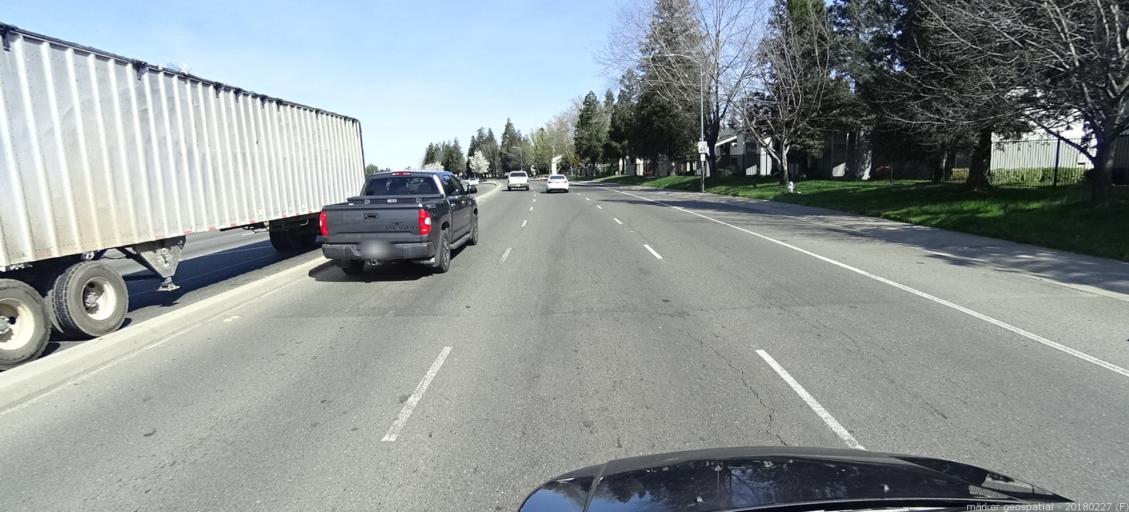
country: US
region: California
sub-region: Sacramento County
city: Rosemont
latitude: 38.5391
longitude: -121.3709
